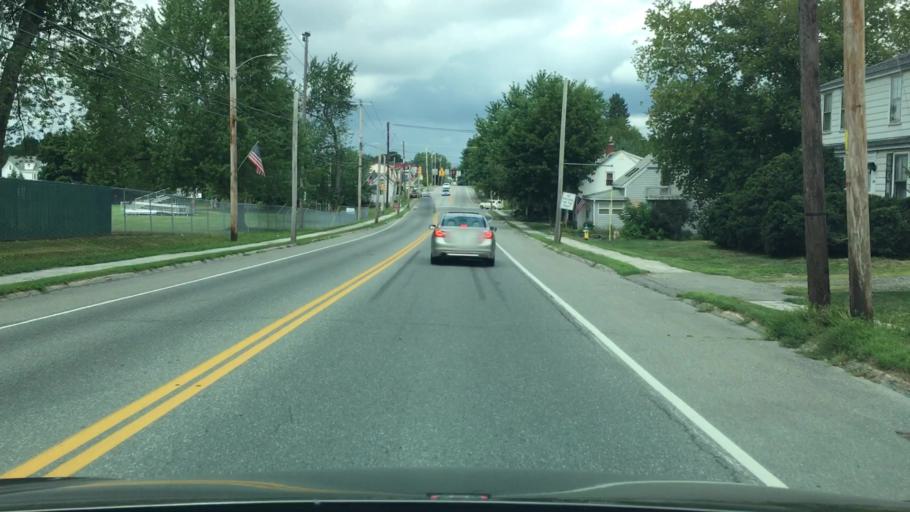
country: US
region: Maine
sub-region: Penobscot County
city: Brewer
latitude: 44.7886
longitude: -68.7551
